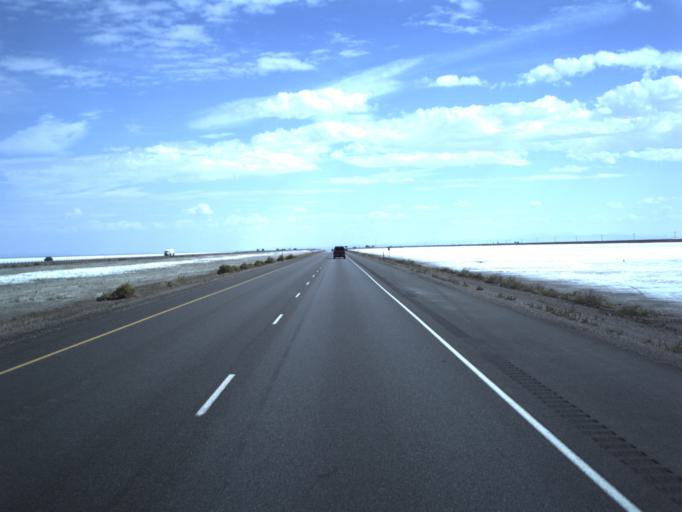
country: US
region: Utah
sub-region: Tooele County
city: Wendover
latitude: 40.7394
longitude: -113.8959
